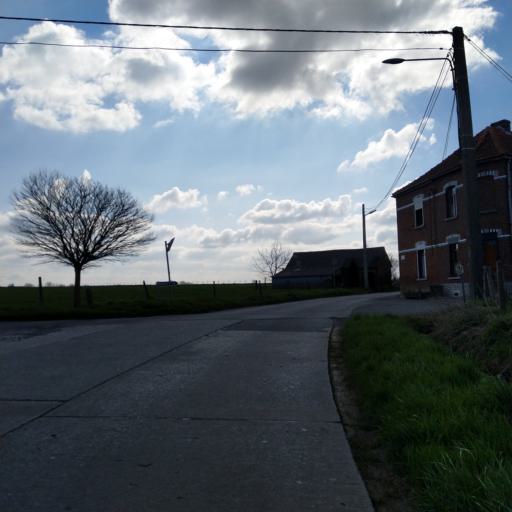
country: BE
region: Wallonia
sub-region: Province du Hainaut
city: Lens
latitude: 50.5761
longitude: 3.9381
